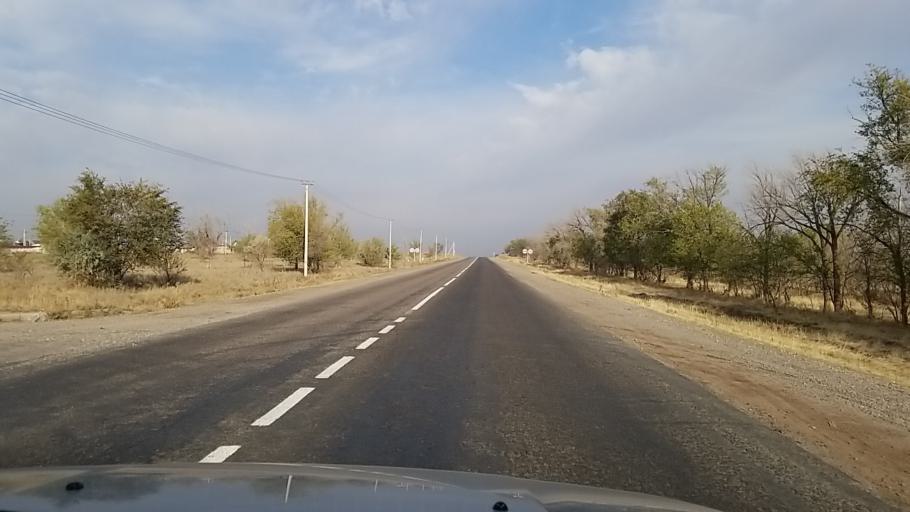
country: KZ
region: Almaty Oblysy
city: Burunday
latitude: 43.4834
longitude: 76.6745
